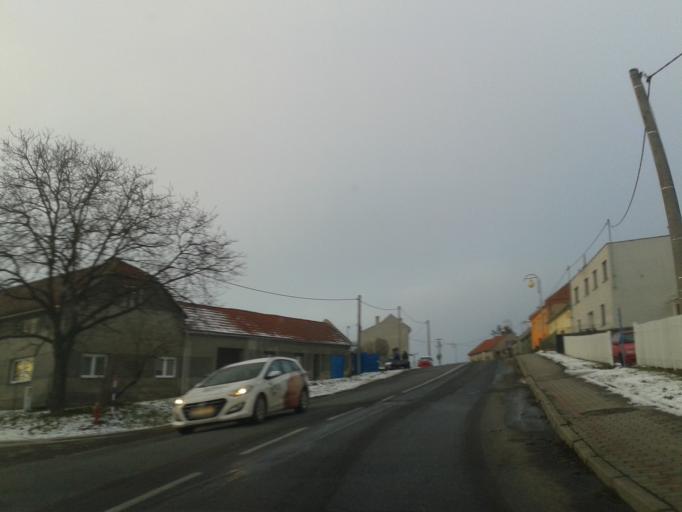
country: CZ
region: Olomoucky
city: Pteni
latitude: 49.4889
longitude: 16.9557
